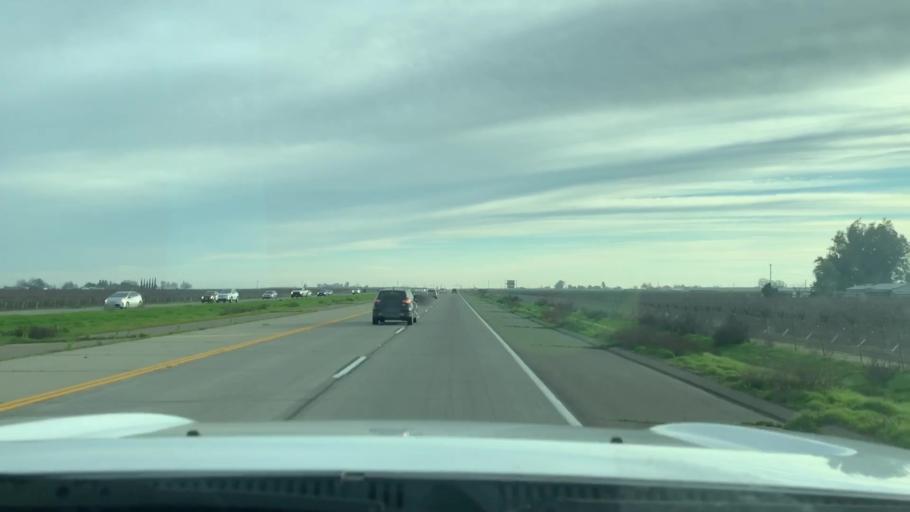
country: US
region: California
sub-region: Fresno County
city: Caruthers
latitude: 36.5570
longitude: -119.7863
